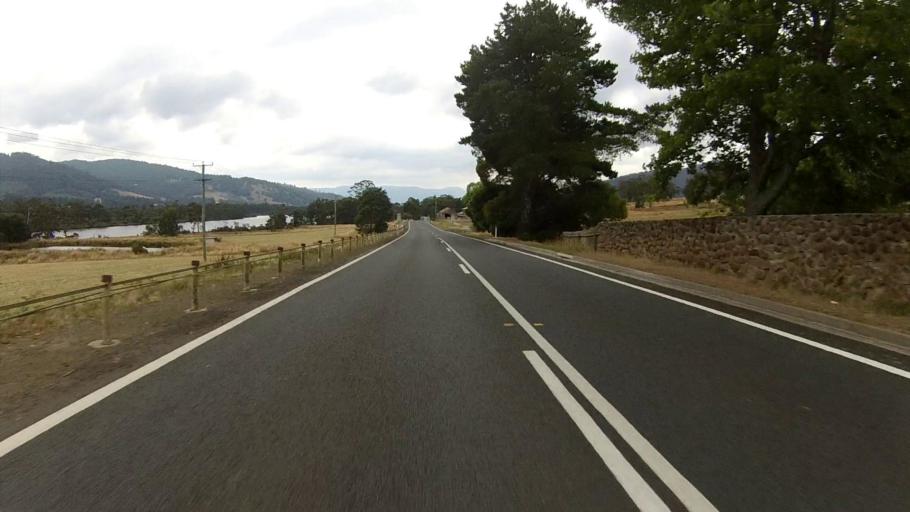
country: AU
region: Tasmania
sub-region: Huon Valley
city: Franklin
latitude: -43.0848
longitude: 147.0300
